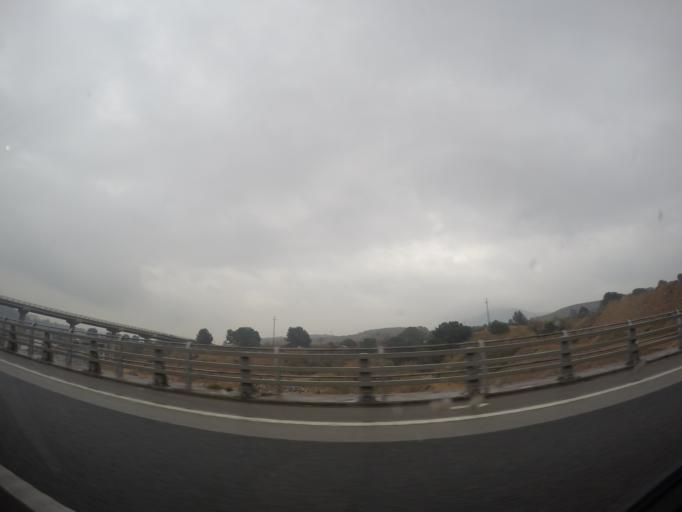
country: ES
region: Catalonia
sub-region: Provincia de Barcelona
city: Palleja
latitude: 41.4440
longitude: 1.9985
